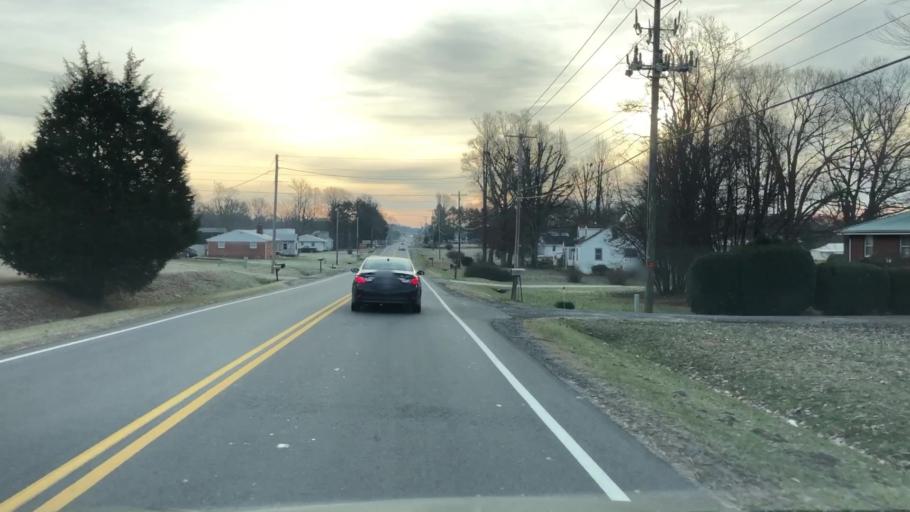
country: US
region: Virginia
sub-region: Campbell County
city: Timberlake
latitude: 37.3327
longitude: -79.2578
